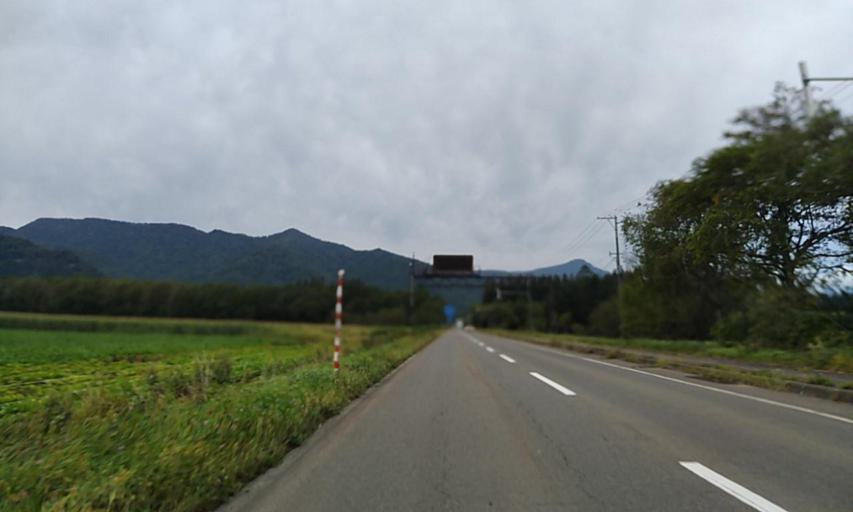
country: JP
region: Hokkaido
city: Bihoro
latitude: 43.5546
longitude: 144.3457
